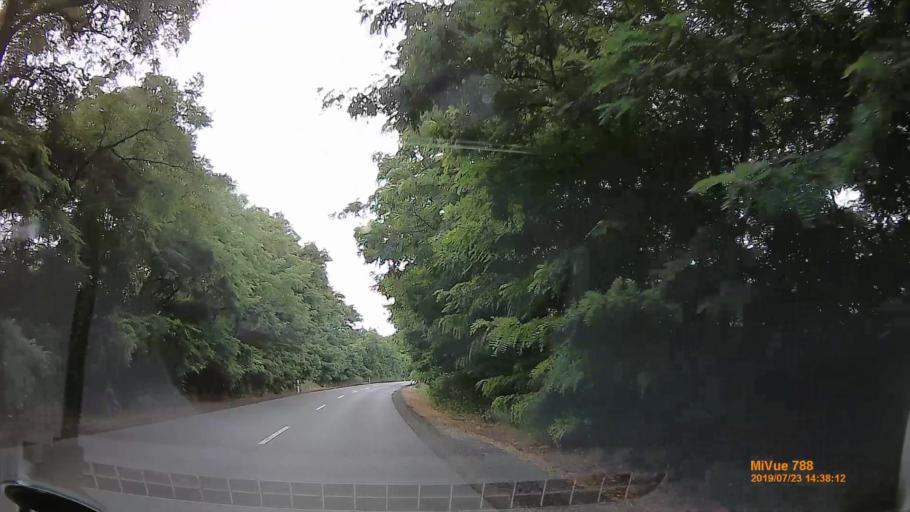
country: HU
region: Szabolcs-Szatmar-Bereg
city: Nyiregyhaza
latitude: 47.9275
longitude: 21.6709
